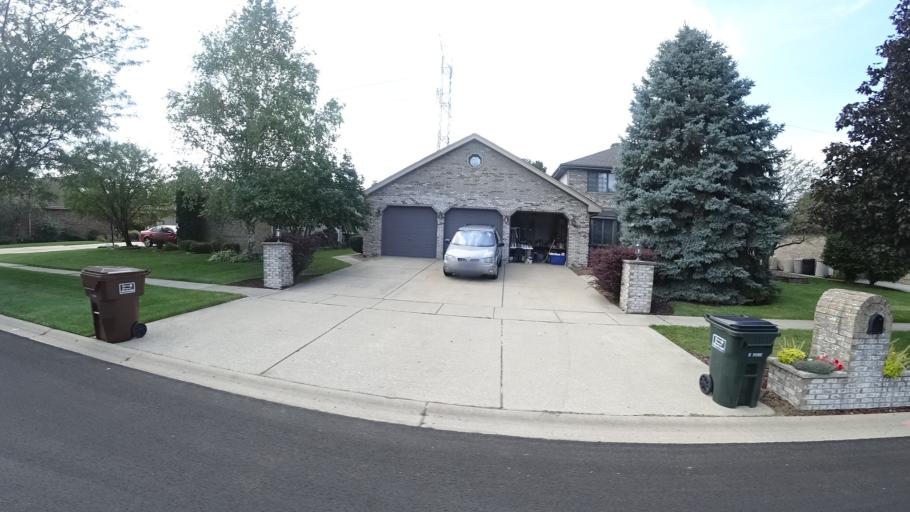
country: US
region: Illinois
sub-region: Cook County
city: Orland Hills
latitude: 41.5663
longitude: -87.8168
